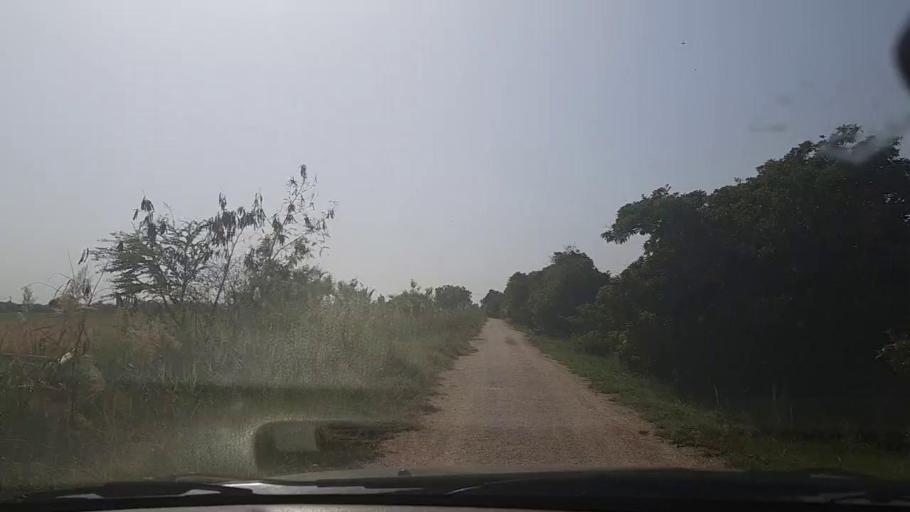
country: PK
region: Sindh
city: Keti Bandar
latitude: 24.1973
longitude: 67.5475
